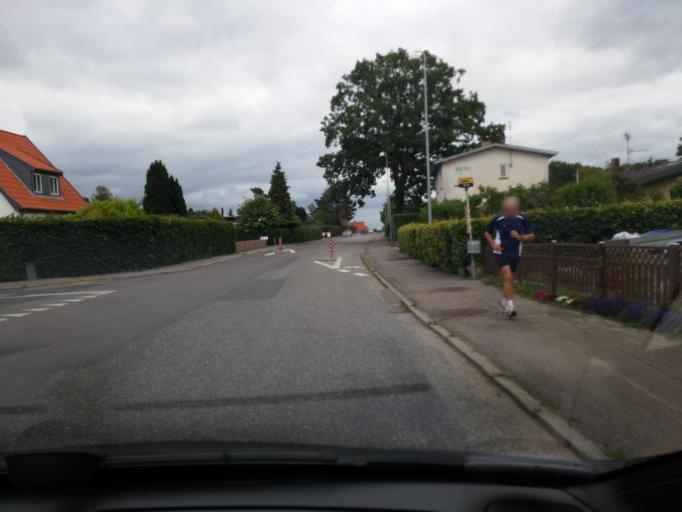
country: DK
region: Capital Region
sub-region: Hillerod Kommune
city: Hillerod
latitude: 55.9376
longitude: 12.3227
